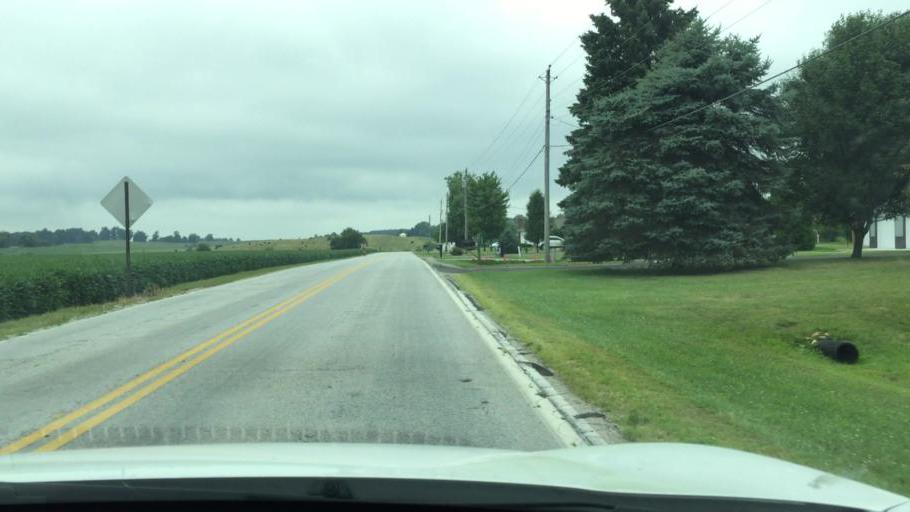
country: US
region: Ohio
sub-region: Clark County
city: Lisbon
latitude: 39.9434
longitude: -83.6819
